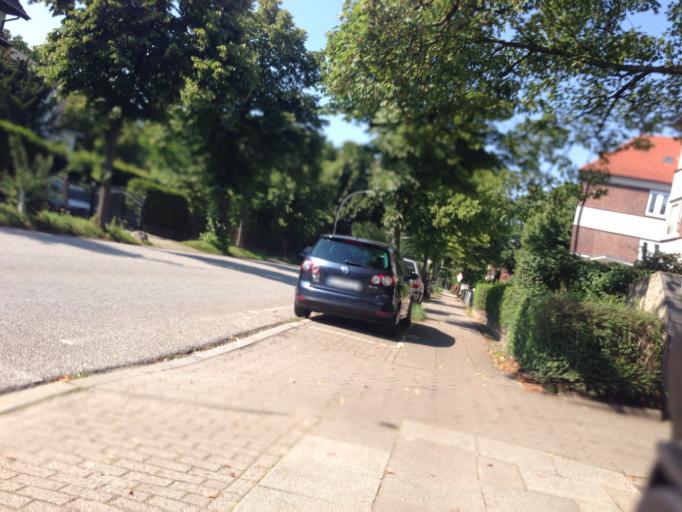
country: DE
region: Hamburg
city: Marienthal
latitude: 53.5695
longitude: 10.0845
